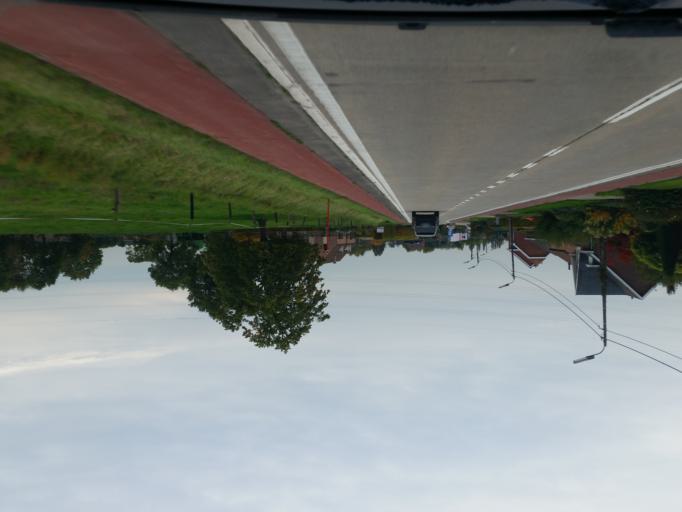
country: BE
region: Flanders
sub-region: Provincie Antwerpen
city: Sint-Katelijne-Waver
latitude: 51.0669
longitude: 4.5630
